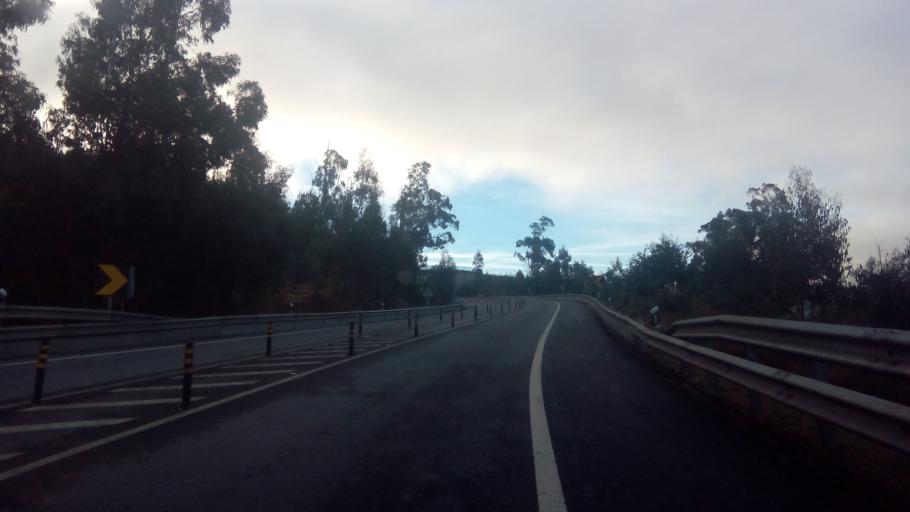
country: PT
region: Porto
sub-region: Amarante
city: Amarante
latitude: 41.2694
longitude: -7.9856
